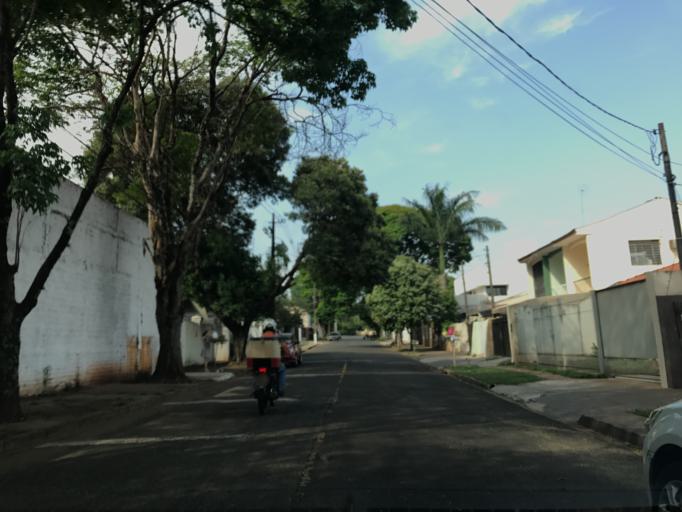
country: BR
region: Parana
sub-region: Maringa
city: Maringa
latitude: -23.4371
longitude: -51.9555
